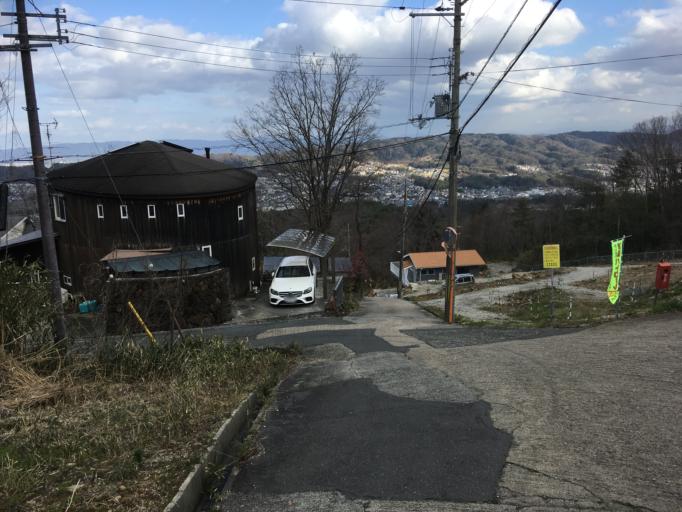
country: JP
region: Nara
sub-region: Ikoma-shi
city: Ikoma
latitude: 34.6756
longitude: 135.6911
